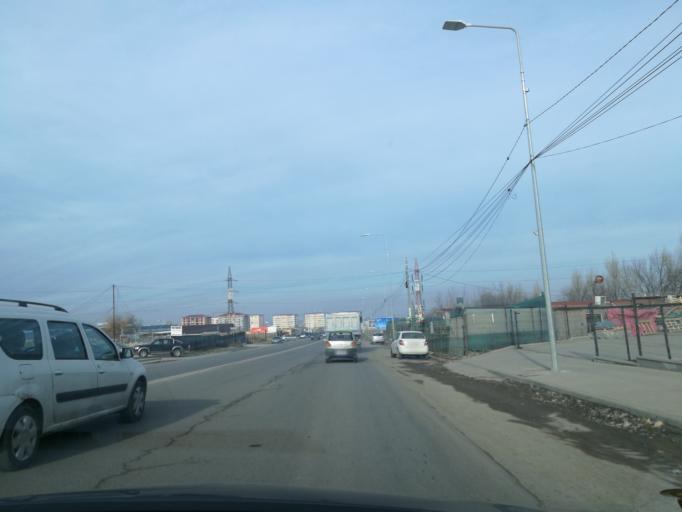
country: RO
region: Constanta
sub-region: Municipiul Constanta
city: Constanta
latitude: 44.1939
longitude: 28.6033
